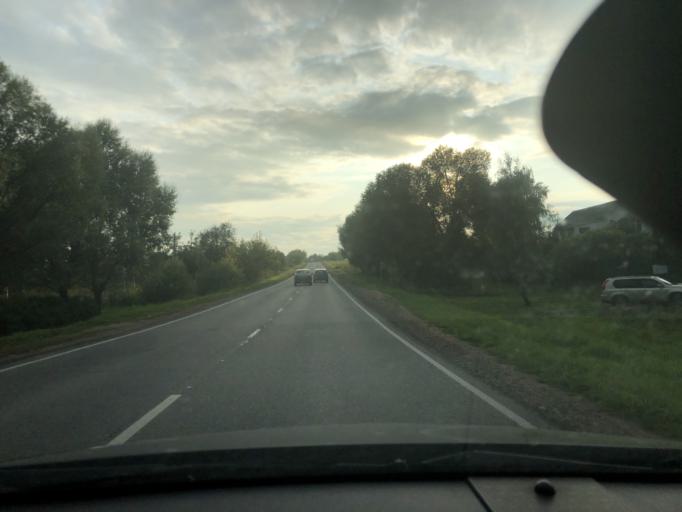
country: RU
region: Tula
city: Leninskiy
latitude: 54.2490
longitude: 37.3403
